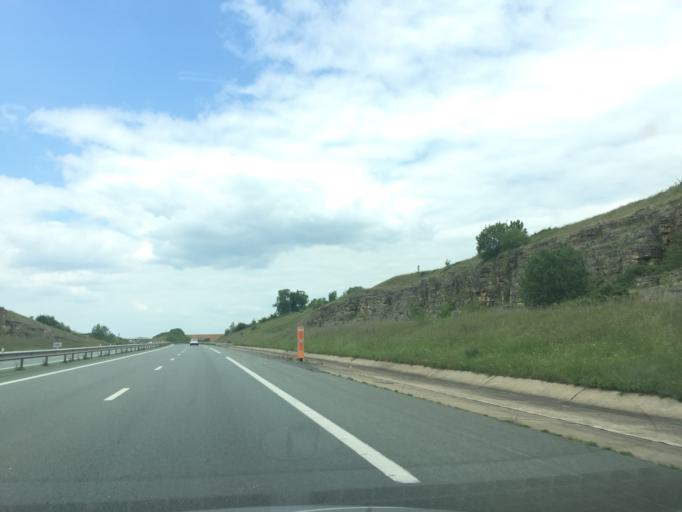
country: FR
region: Poitou-Charentes
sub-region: Departement des Deux-Sevres
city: Chauray
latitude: 46.3801
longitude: -0.3629
